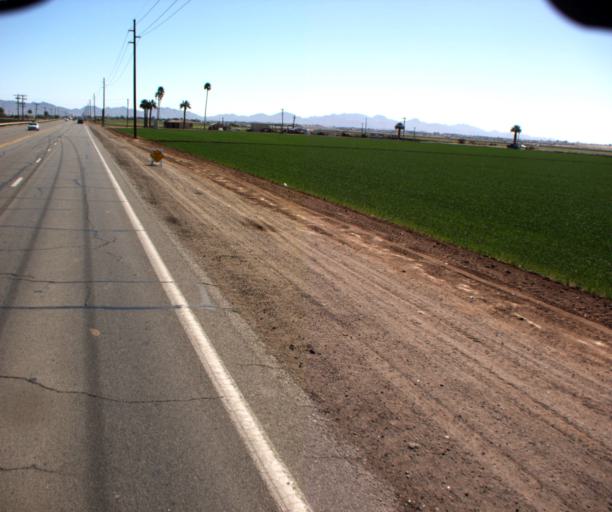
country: US
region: Arizona
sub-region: Yuma County
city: Yuma
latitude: 32.6988
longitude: -114.5671
